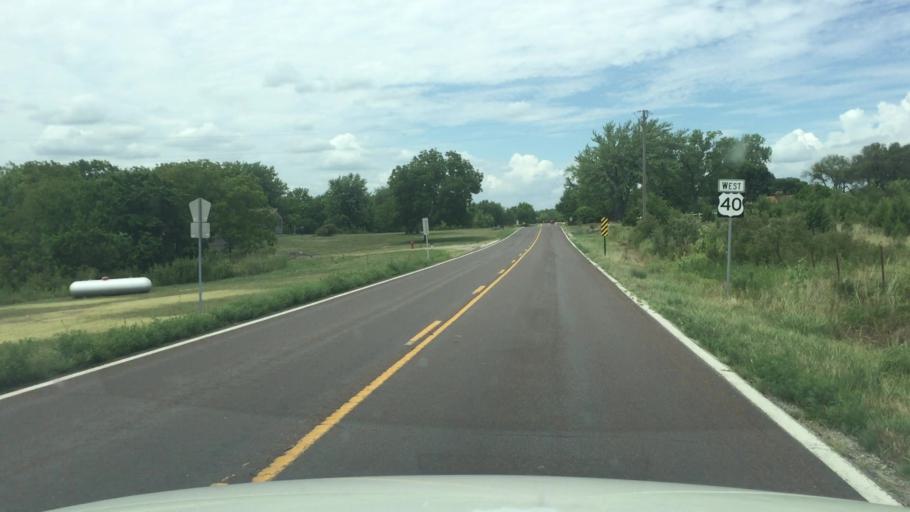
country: US
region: Kansas
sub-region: Douglas County
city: Lawrence
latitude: 38.9951
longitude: -95.3997
